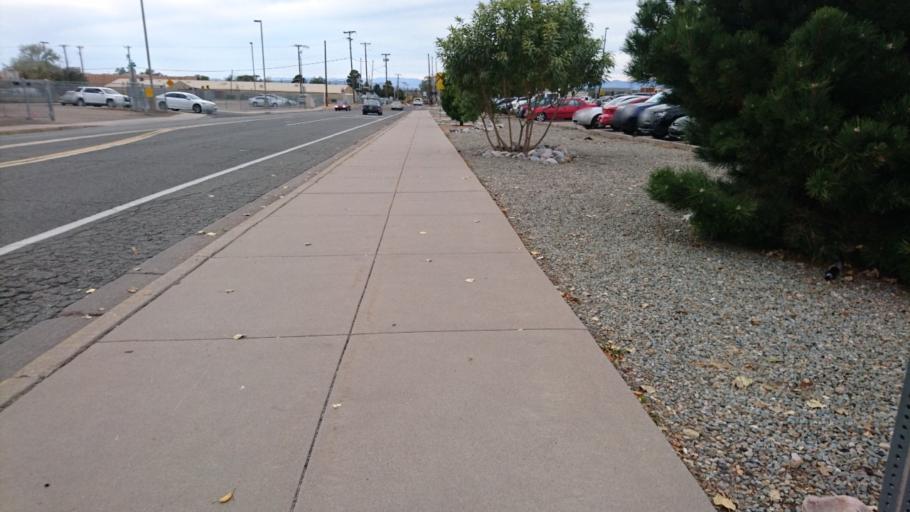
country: US
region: New Mexico
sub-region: Santa Fe County
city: Santa Fe
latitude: 35.6715
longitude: -105.9567
